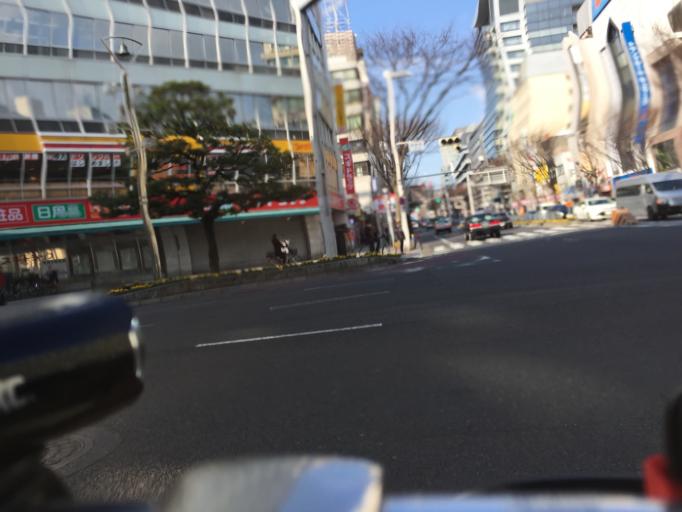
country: JP
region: Aichi
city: Nagoya-shi
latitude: 35.1693
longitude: 136.9147
